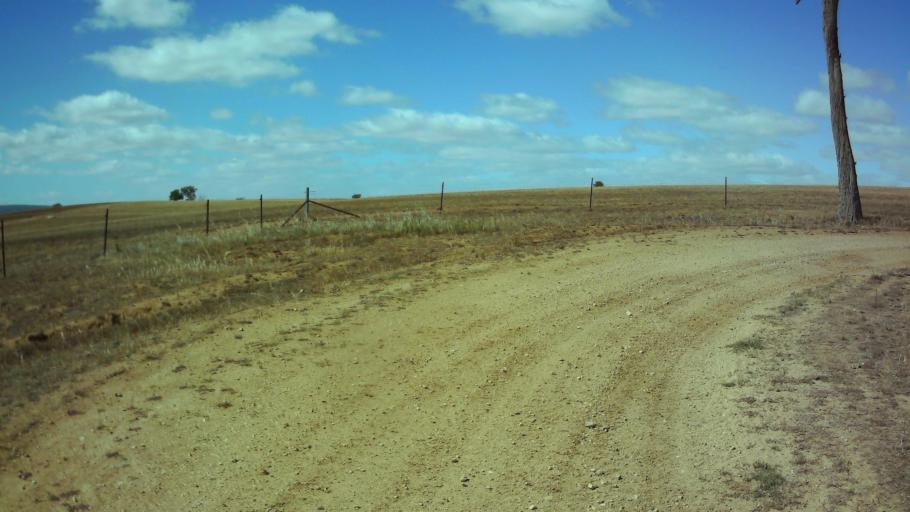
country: AU
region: New South Wales
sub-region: Weddin
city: Grenfell
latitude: -33.9798
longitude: 148.3881
